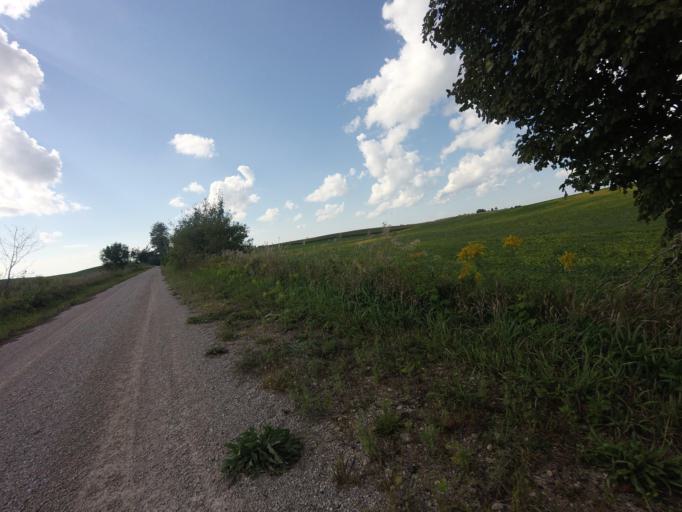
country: CA
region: Ontario
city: Huron East
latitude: 43.7422
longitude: -81.4829
